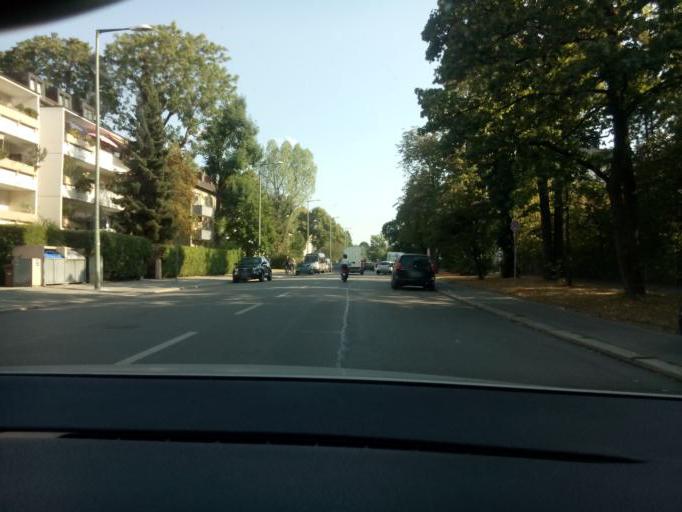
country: DE
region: Bavaria
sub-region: Upper Bavaria
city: Unterhaching
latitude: 48.1040
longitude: 11.6058
